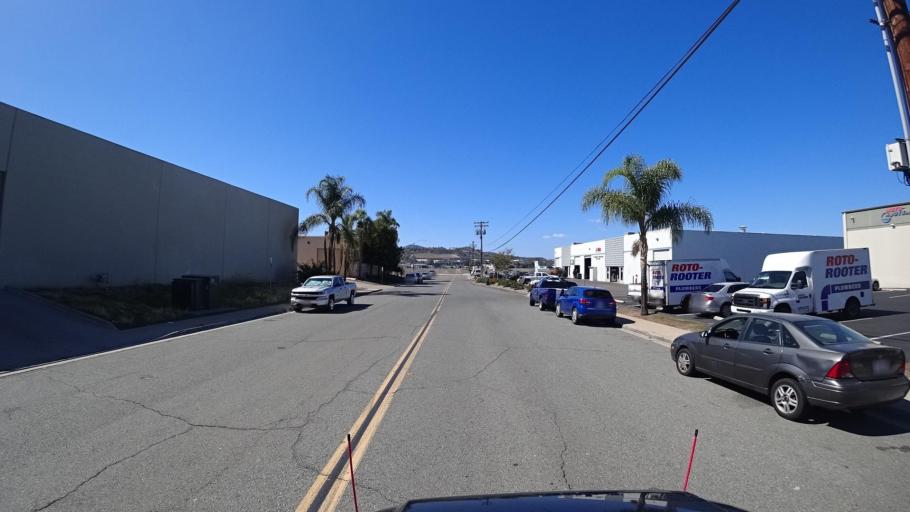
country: US
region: California
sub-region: San Diego County
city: Santee
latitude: 32.8206
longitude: -116.9638
